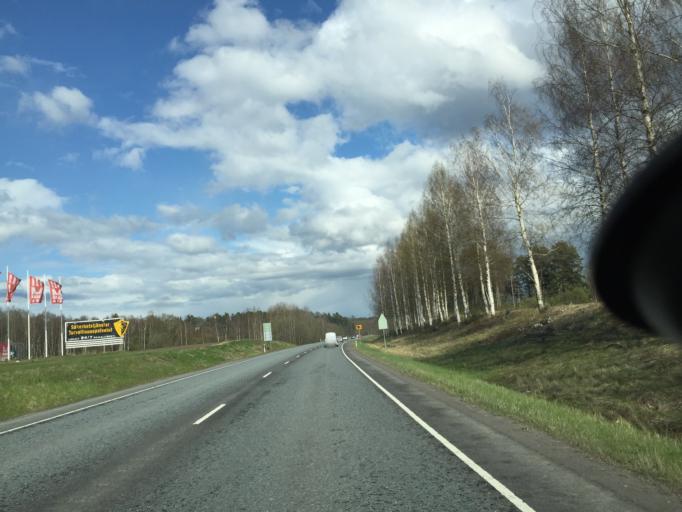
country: FI
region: Uusimaa
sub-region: Raaseporin
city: Karis
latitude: 60.0544
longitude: 23.6524
